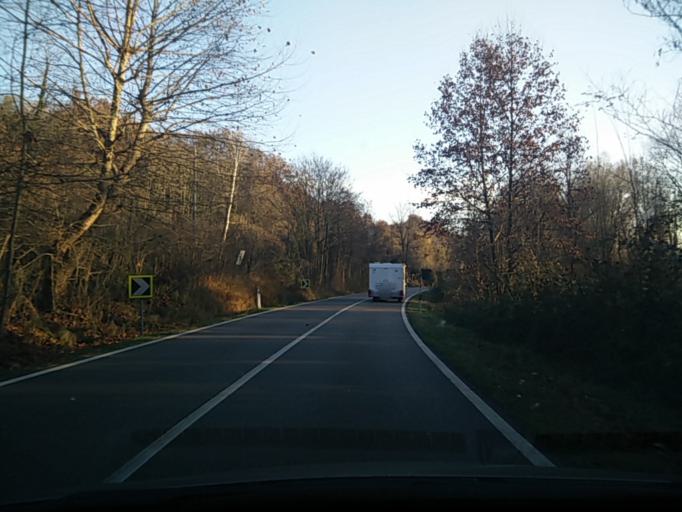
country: IT
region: Veneto
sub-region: Provincia di Verona
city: Salionze
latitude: 45.4189
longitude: 10.7150
